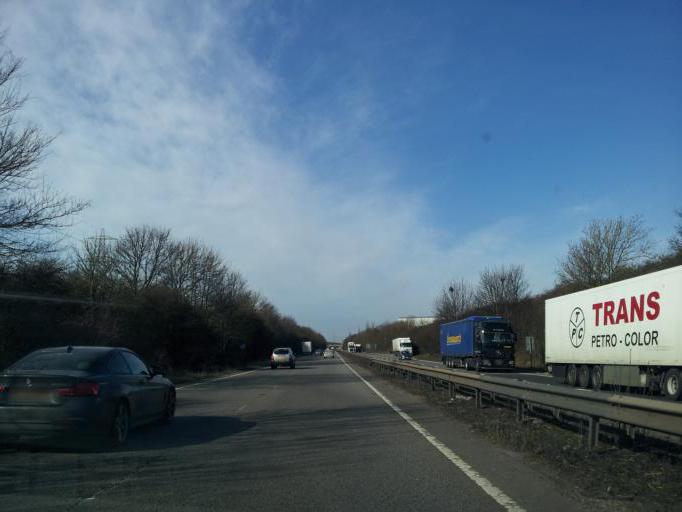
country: GB
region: England
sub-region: Lincolnshire
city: Barrowby
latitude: 52.9016
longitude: -0.6698
